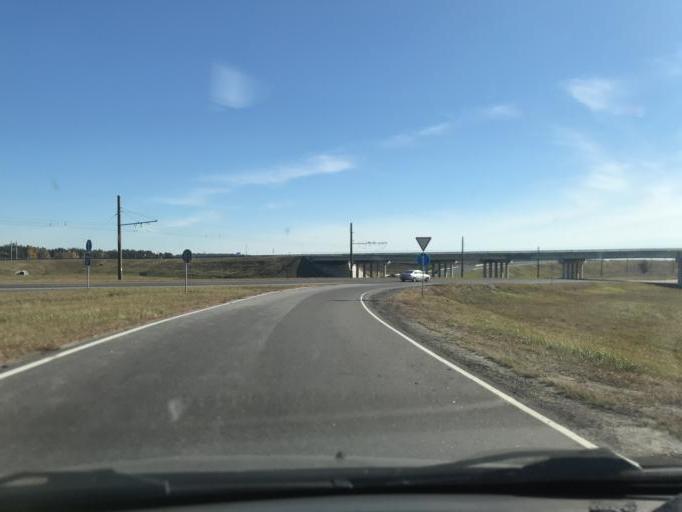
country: BY
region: Gomel
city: Mazyr
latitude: 52.0104
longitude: 29.2524
